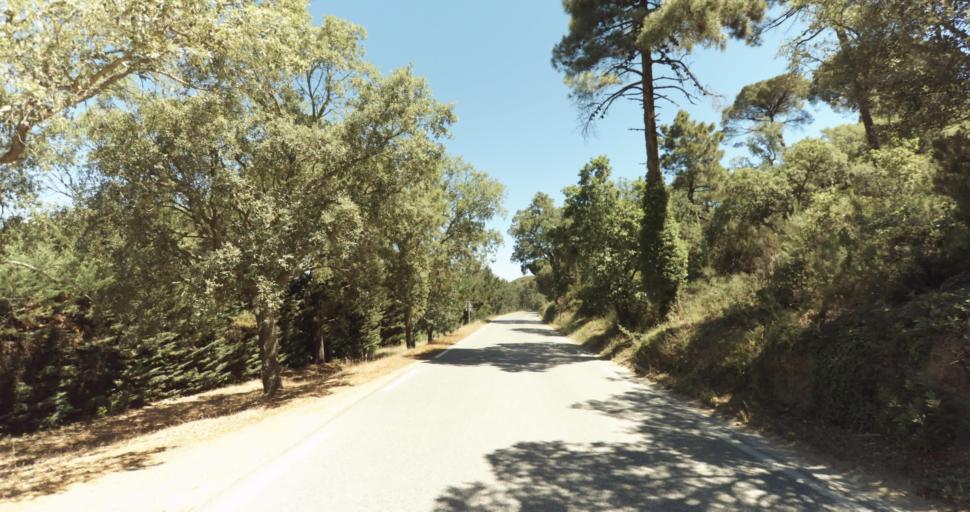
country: FR
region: Provence-Alpes-Cote d'Azur
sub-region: Departement du Var
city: Gassin
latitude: 43.2490
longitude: 6.5809
